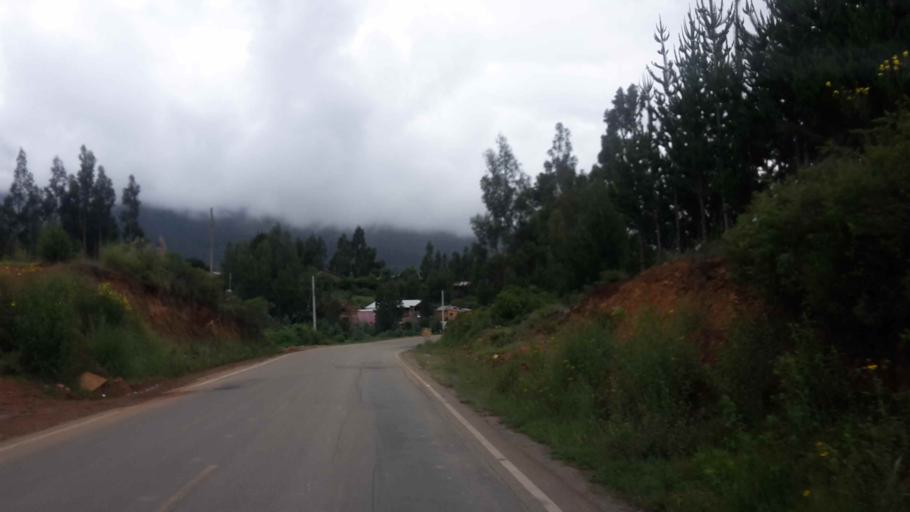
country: BO
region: Cochabamba
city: Totora
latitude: -17.5802
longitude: -65.3094
